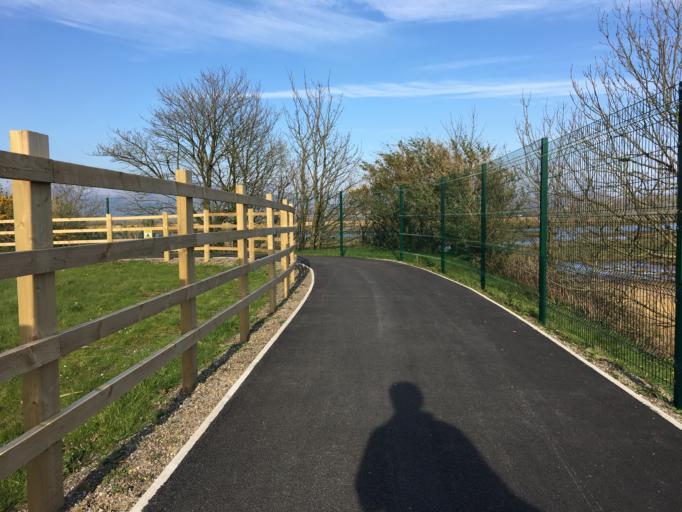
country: GB
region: Wales
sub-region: Gwynedd
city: Porthmadog
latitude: 52.9241
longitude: -4.1247
